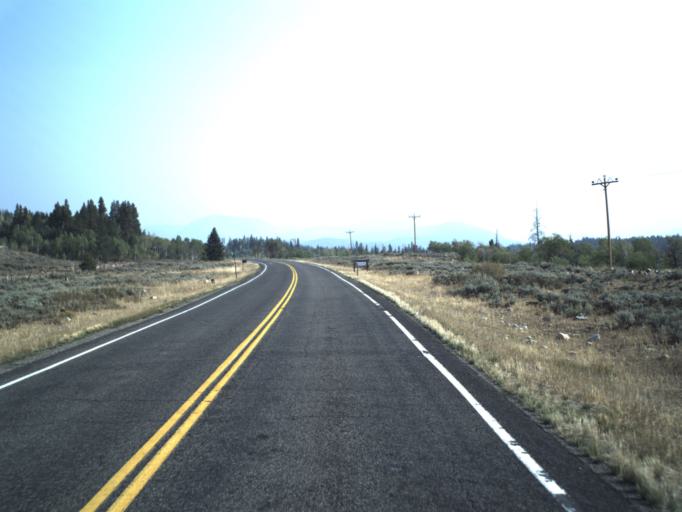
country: US
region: Wyoming
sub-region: Uinta County
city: Evanston
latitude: 40.9364
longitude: -110.8355
